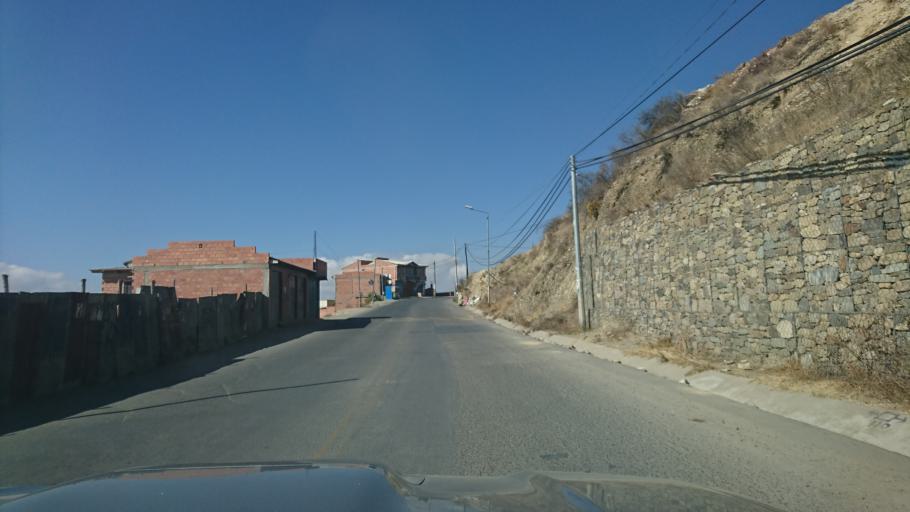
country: BO
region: La Paz
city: La Paz
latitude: -16.5110
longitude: -68.1027
